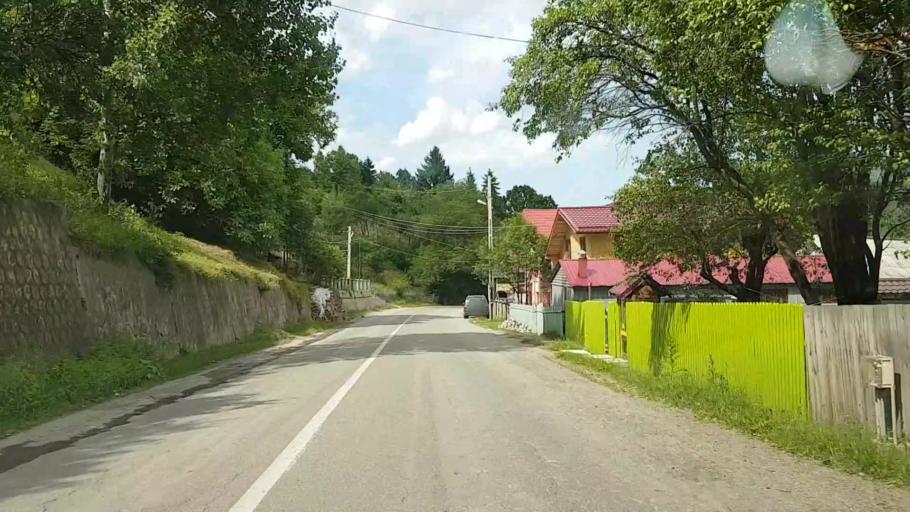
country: RO
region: Neamt
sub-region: Comuna Hangu
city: Hangu
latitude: 47.0530
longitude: 26.0281
